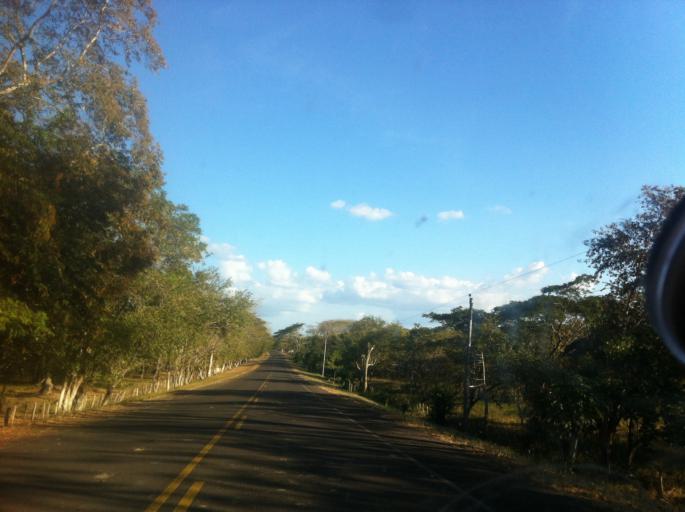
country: NI
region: Rio San Juan
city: Morrito
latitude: 11.7382
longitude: -84.9827
